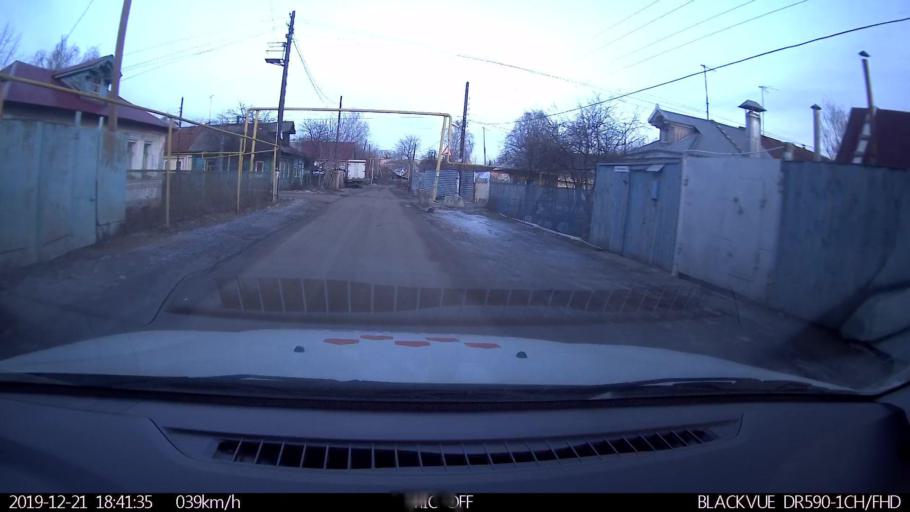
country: RU
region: Nizjnij Novgorod
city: Nizhniy Novgorod
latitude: 56.3287
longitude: 43.9252
